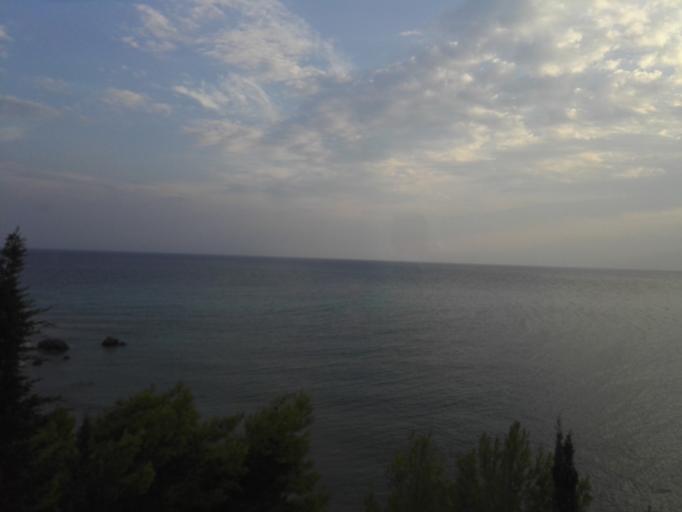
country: IT
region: Calabria
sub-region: Provincia di Reggio Calabria
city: Bova Marina
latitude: 37.9272
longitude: 15.9348
